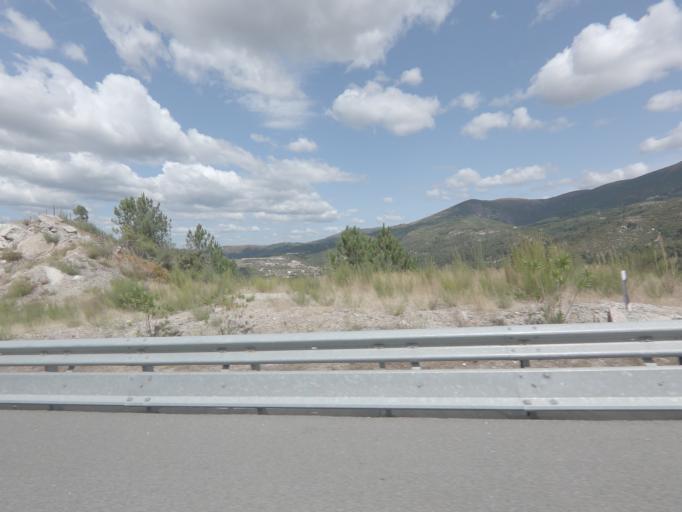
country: PT
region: Porto
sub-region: Amarante
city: Amarante
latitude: 41.2499
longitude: -7.9926
